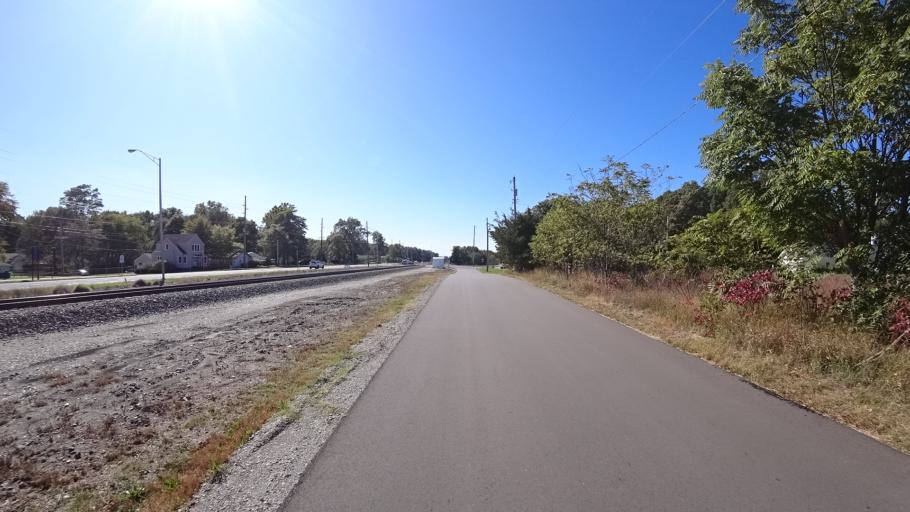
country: US
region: Indiana
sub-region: LaPorte County
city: Long Beach
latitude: 41.7449
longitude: -86.8296
